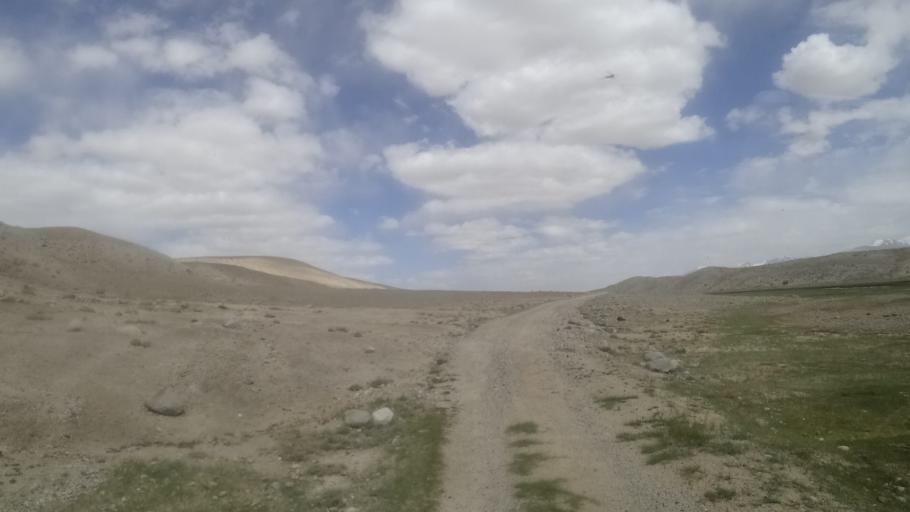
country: AF
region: Badakhshan
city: Khandud
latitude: 37.4087
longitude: 73.1566
